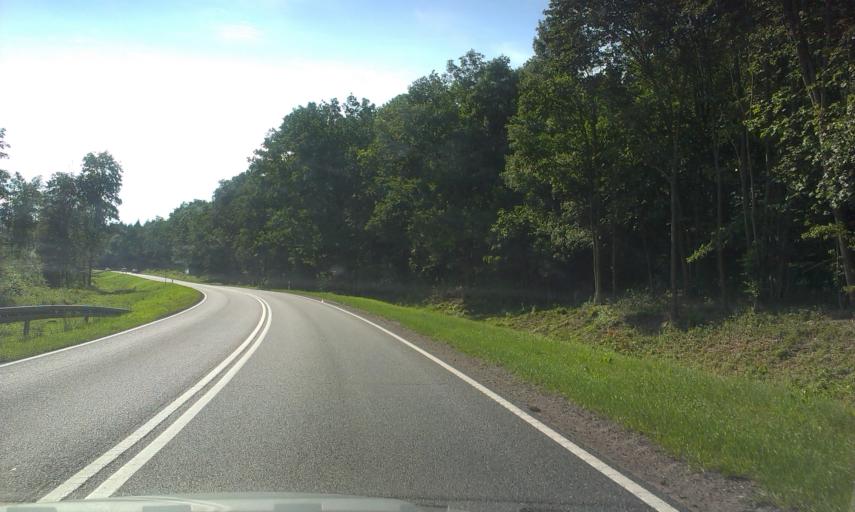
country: PL
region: Kujawsko-Pomorskie
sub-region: Powiat bydgoski
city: Sicienko
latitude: 53.1614
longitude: 17.8095
